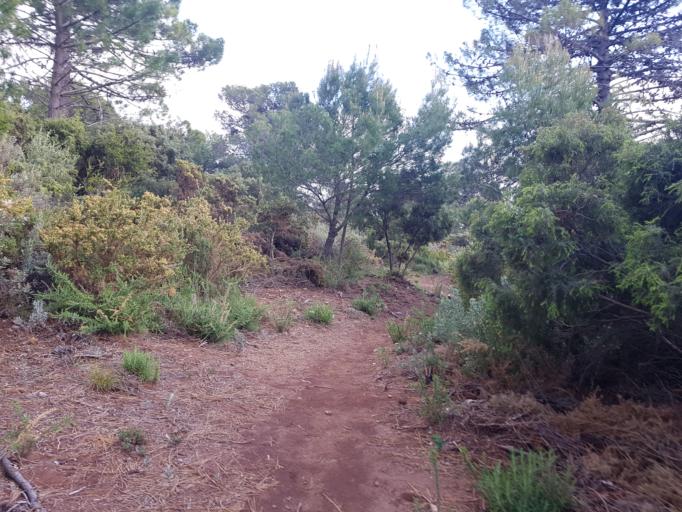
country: ES
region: Andalusia
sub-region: Provincia de Malaga
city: Marbella
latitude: 36.5522
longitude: -4.8937
